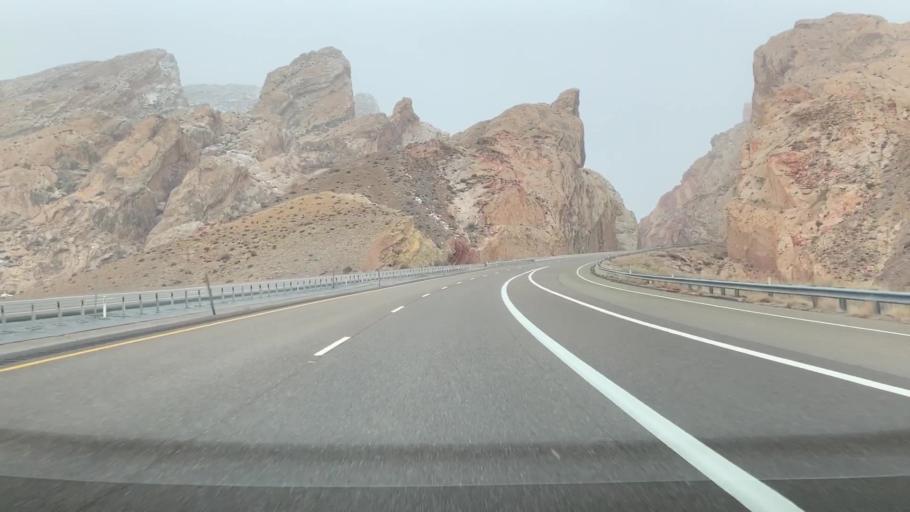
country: US
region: Utah
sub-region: Carbon County
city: East Carbon City
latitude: 38.9196
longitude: -110.4355
